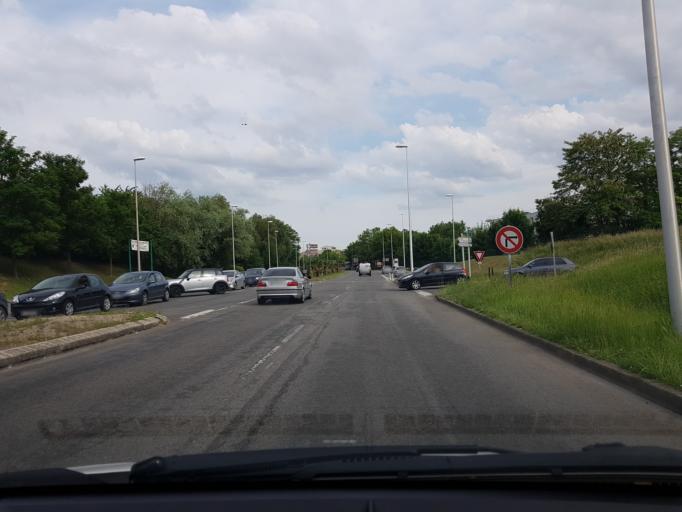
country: FR
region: Ile-de-France
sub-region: Departement de Seine-et-Marne
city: Torcy
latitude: 48.8458
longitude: 2.6469
